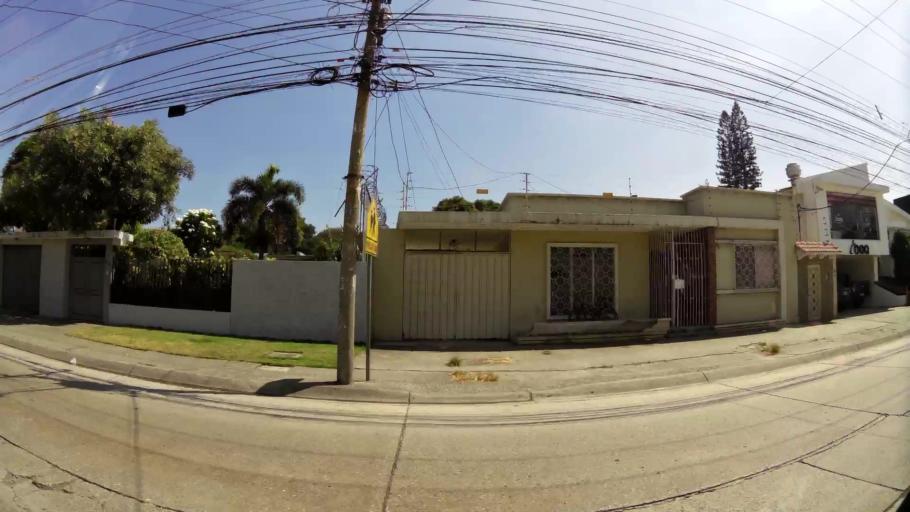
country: EC
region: Guayas
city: Guayaquil
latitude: -2.1738
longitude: -79.9098
